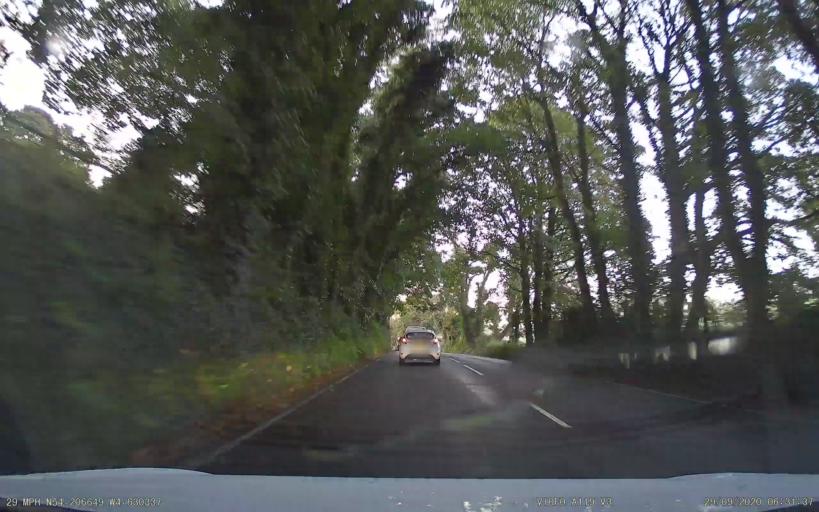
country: IM
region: Castletown
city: Castletown
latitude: 54.2066
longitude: -4.6303
